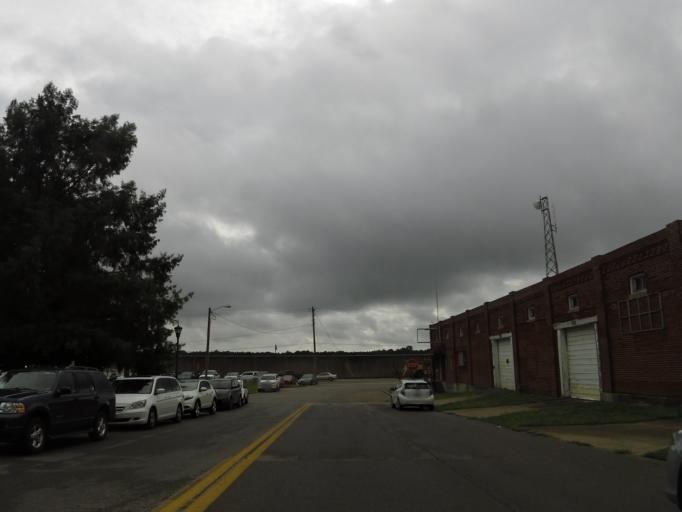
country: US
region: Missouri
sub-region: Cape Girardeau County
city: Cape Girardeau
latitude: 37.3003
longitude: -89.5197
